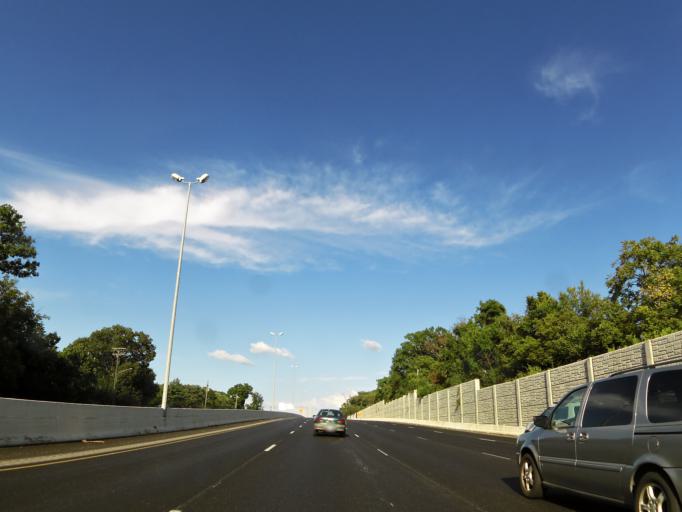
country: US
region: Tennessee
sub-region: Davidson County
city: Lakewood
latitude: 36.2342
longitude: -86.7181
